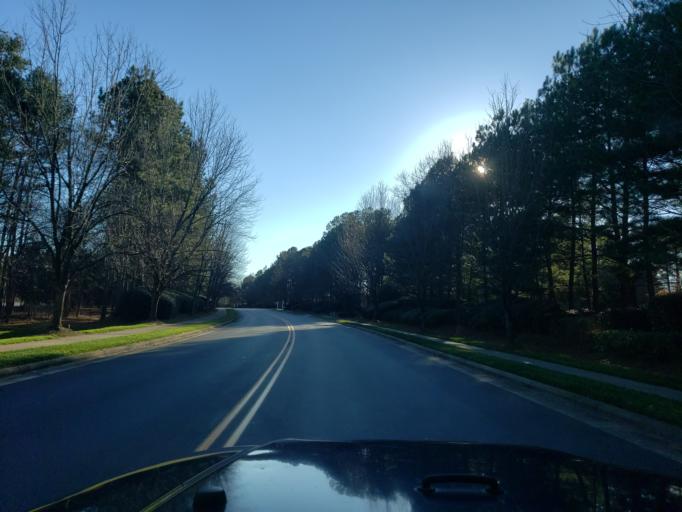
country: US
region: North Carolina
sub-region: Catawba County
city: Lake Norman of Catawba
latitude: 35.5335
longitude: -80.9219
